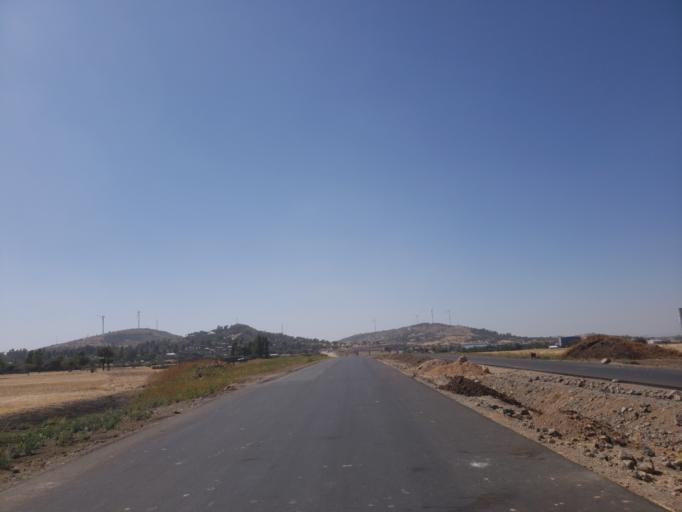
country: ET
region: Oromiya
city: Mojo
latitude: 8.5742
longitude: 39.1696
